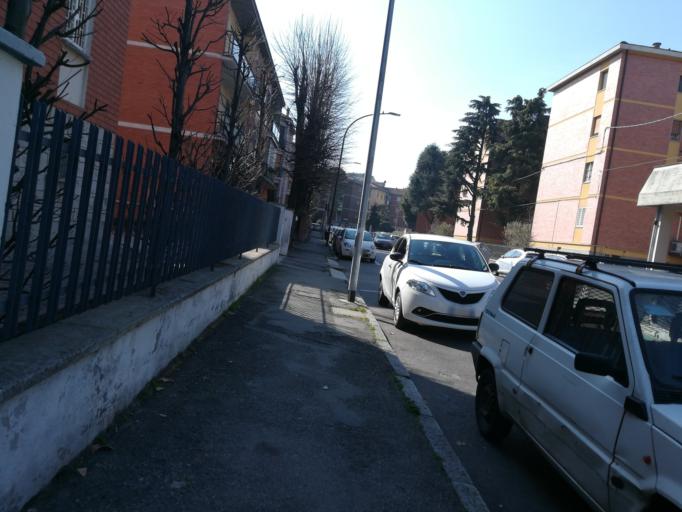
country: IT
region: Emilia-Romagna
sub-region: Provincia di Bologna
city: Progresso
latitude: 44.5419
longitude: 11.3587
